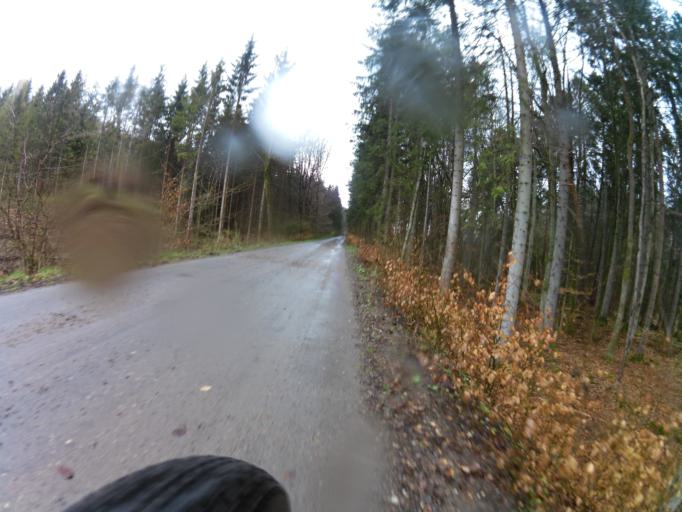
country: PL
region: Pomeranian Voivodeship
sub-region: Powiat slupski
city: Kepice
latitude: 54.2699
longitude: 16.7975
